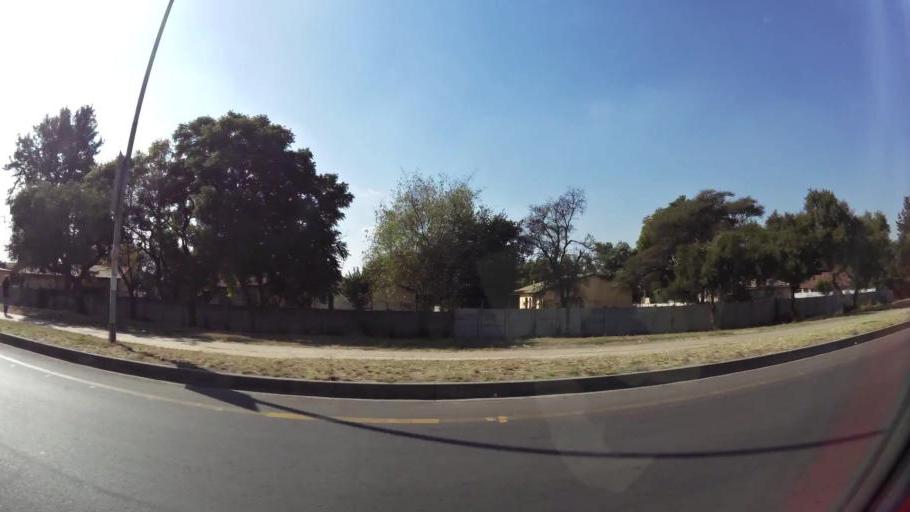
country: ZA
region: North-West
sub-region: Bojanala Platinum District Municipality
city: Rustenburg
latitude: -25.6585
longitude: 27.2265
